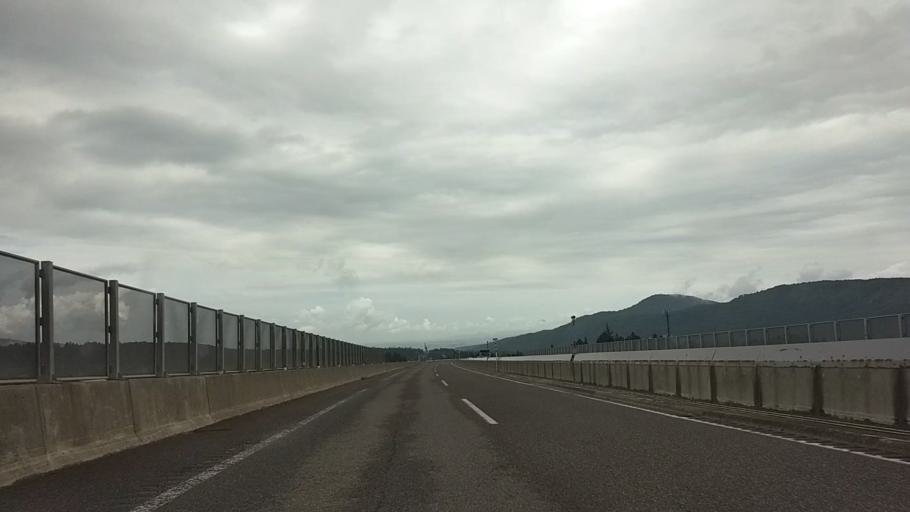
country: JP
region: Niigata
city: Arai
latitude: 36.9449
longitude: 138.2139
